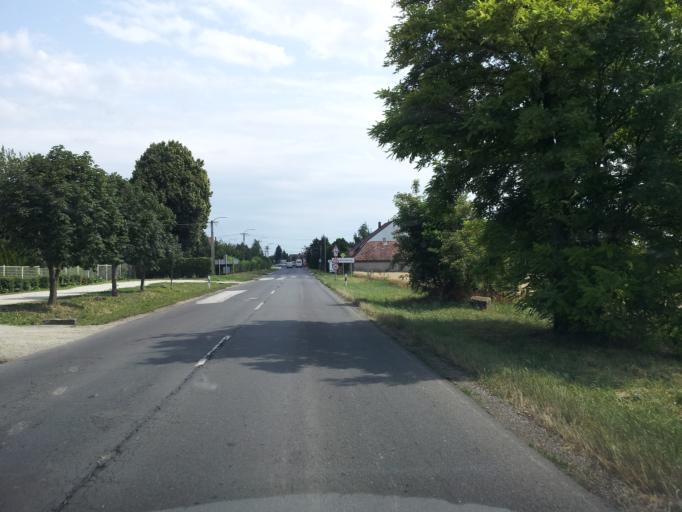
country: HU
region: Fejer
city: Enying
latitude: 46.9590
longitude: 18.2149
